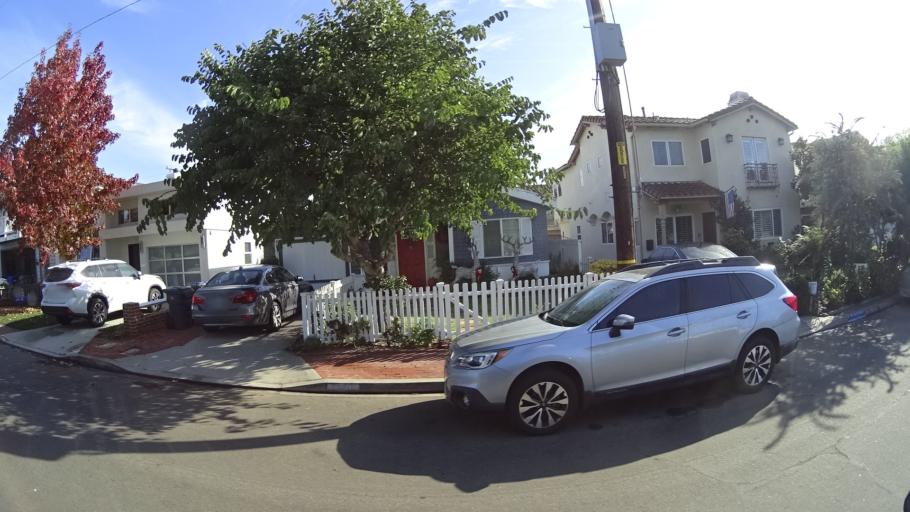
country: US
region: California
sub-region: Los Angeles County
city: Manhattan Beach
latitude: 33.8896
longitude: -118.4005
